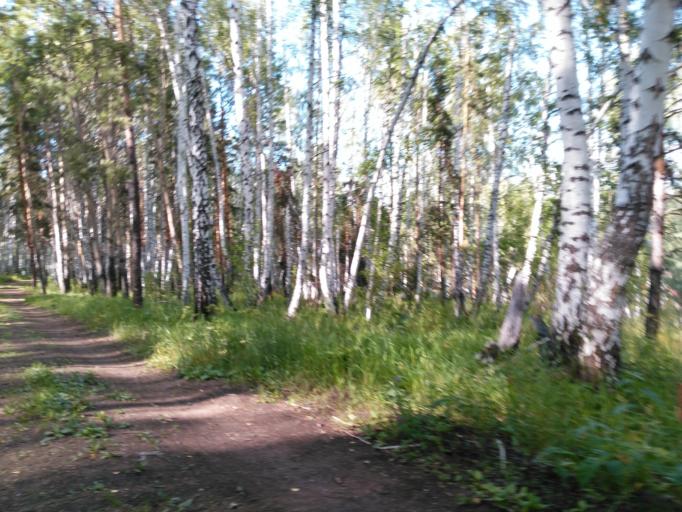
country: RU
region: Bashkortostan
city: Uchaly
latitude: 54.3310
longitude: 59.3579
